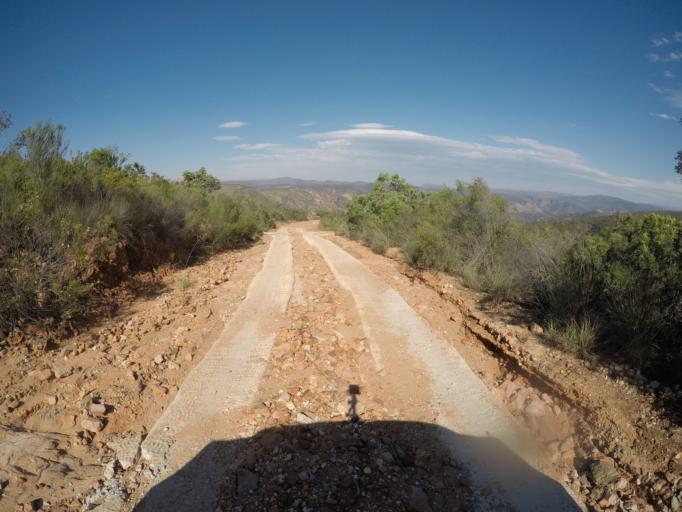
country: ZA
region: Eastern Cape
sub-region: Cacadu District Municipality
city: Kareedouw
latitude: -33.6366
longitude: 24.4495
